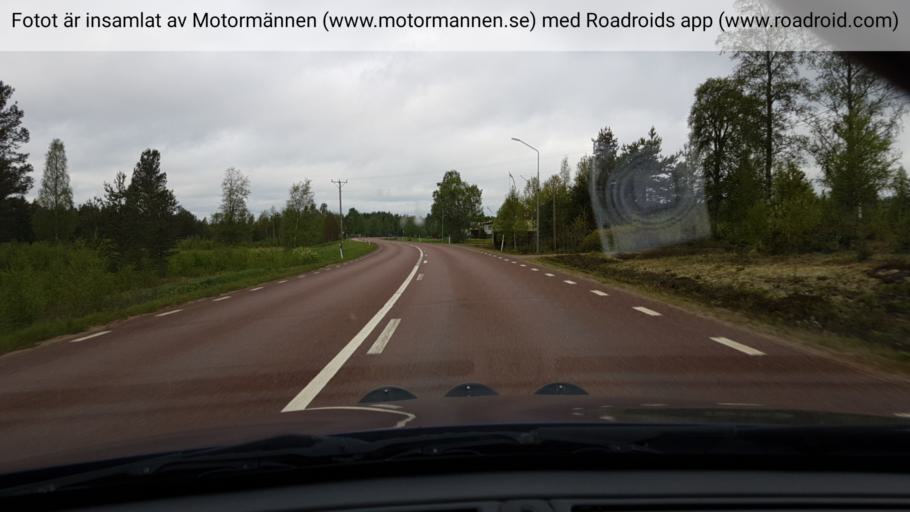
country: SE
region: Jaemtland
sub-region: Harjedalens Kommun
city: Sveg
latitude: 62.0439
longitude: 14.7232
